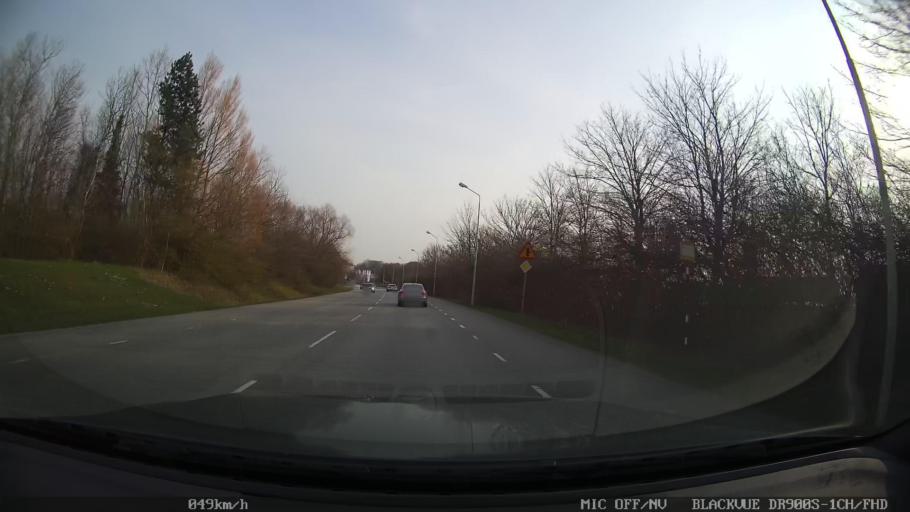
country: SE
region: Skane
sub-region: Ystads Kommun
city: Ystad
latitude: 55.4408
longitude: 13.8072
